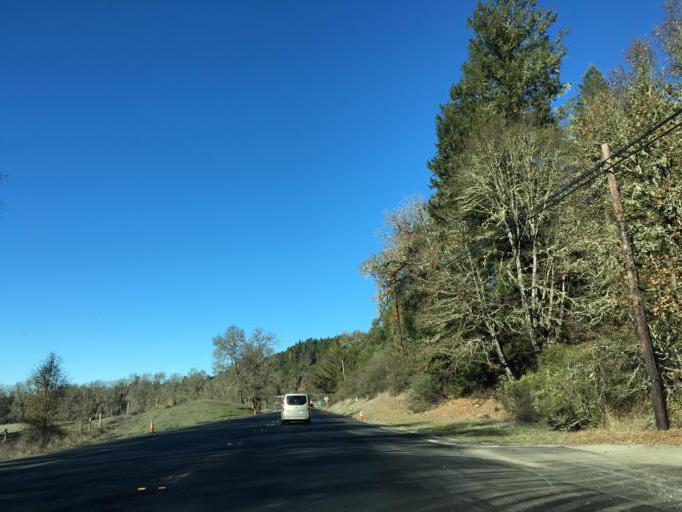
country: US
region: California
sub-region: Mendocino County
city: Laytonville
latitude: 39.6771
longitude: -123.4758
